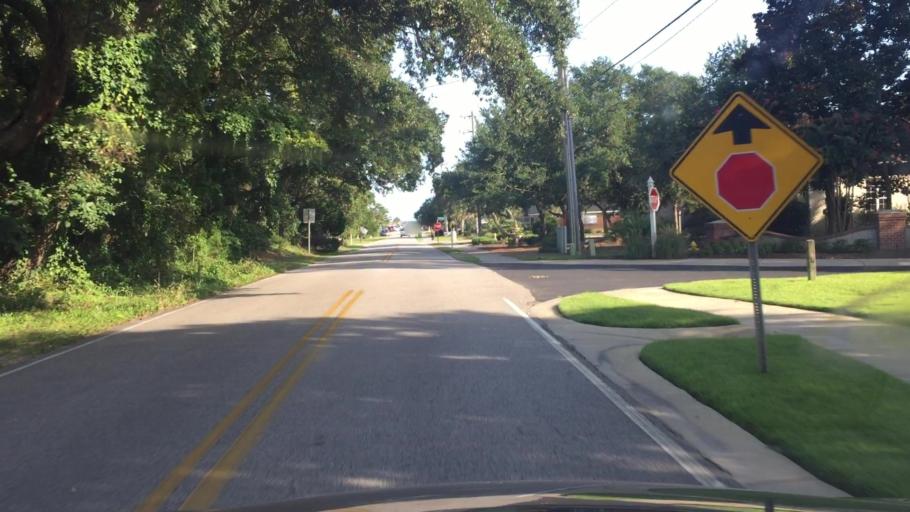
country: US
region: South Carolina
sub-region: Horry County
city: North Myrtle Beach
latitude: 33.8244
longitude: -78.6642
